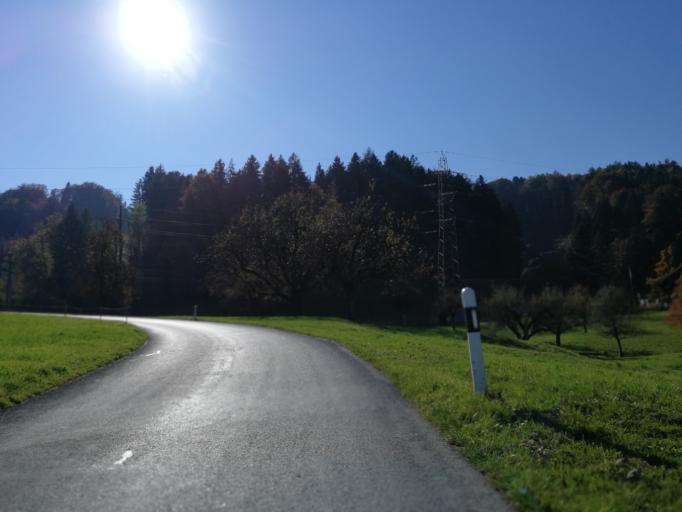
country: CH
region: Schwyz
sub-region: Bezirk March
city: Altendorf
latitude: 47.1832
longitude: 8.8277
